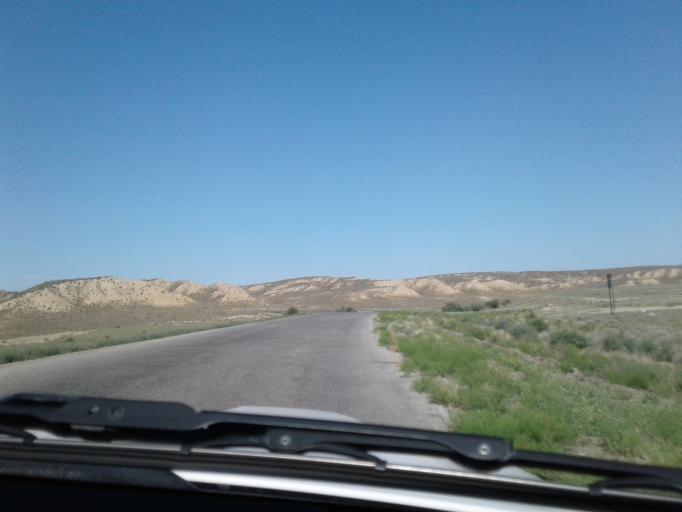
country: TM
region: Balkan
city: Magtymguly
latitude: 38.6505
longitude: 56.2716
